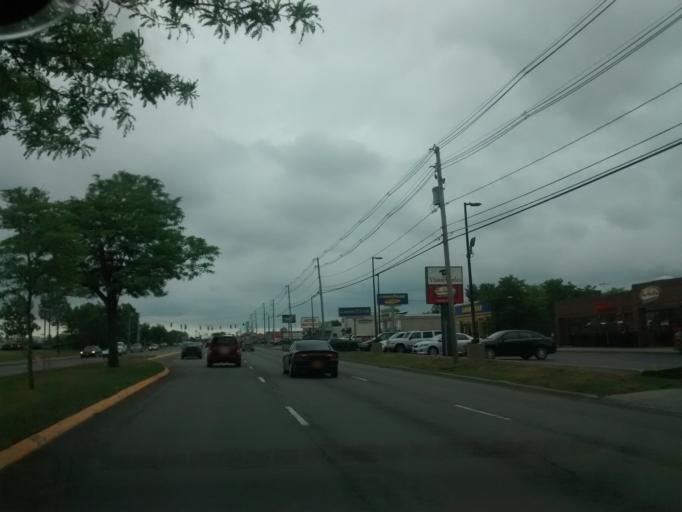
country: US
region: New York
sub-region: Erie County
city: Amherst
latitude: 42.9899
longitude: -78.8227
